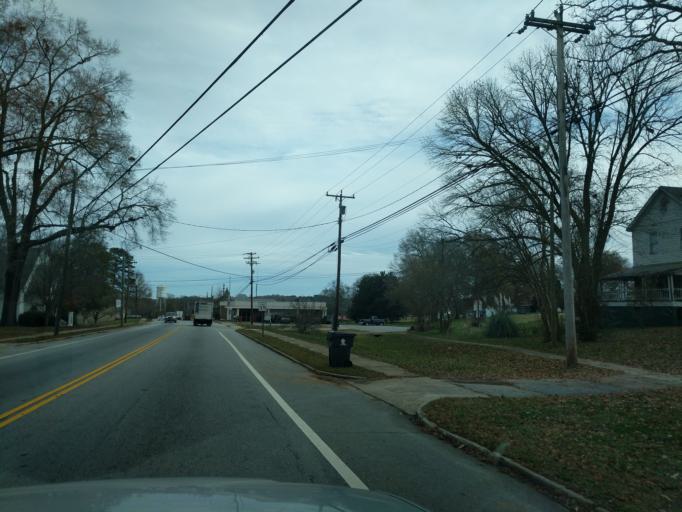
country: US
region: South Carolina
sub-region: Anderson County
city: Williamston
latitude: 34.6425
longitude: -82.4618
